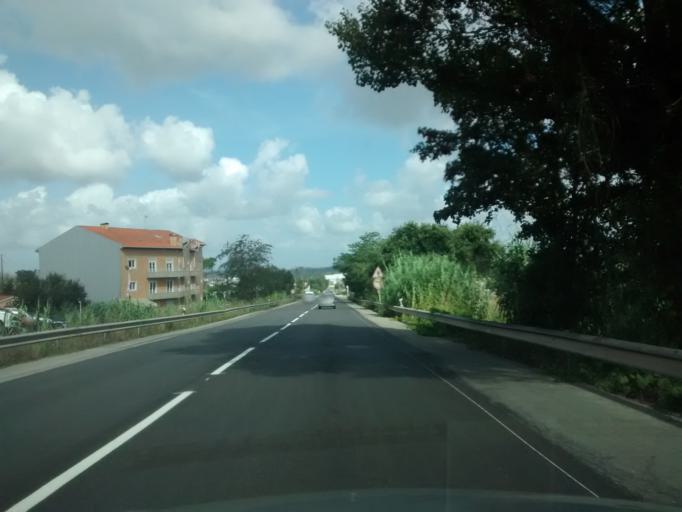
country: PT
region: Aveiro
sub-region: Oliveira do Bairro
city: Oia
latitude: 40.5492
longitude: -8.5415
